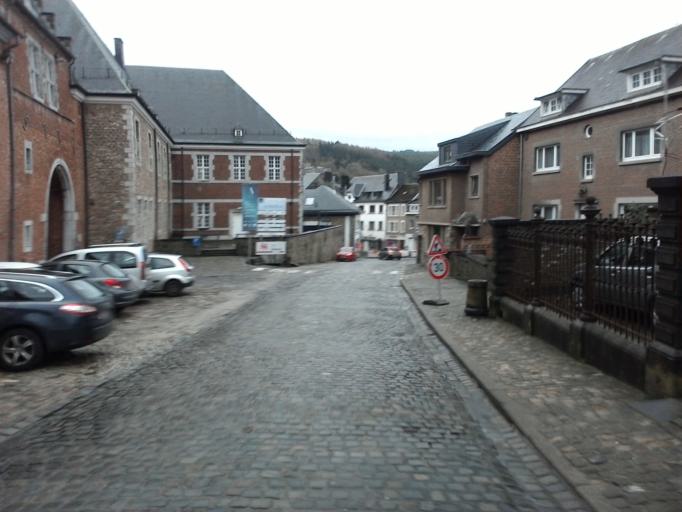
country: BE
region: Wallonia
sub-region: Province de Liege
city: Stavelot
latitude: 50.3933
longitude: 5.9307
